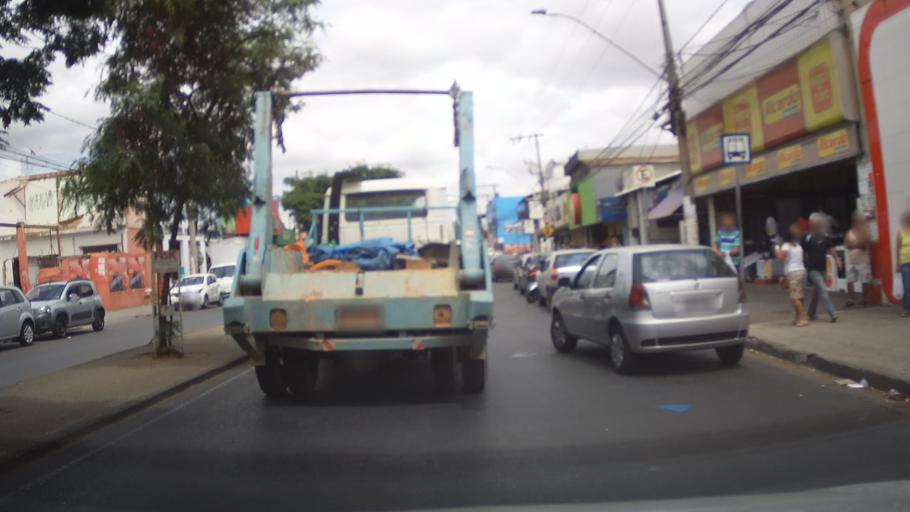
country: BR
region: Minas Gerais
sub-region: Ribeirao Das Neves
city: Ribeirao das Neves
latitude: -19.8030
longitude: -43.9982
